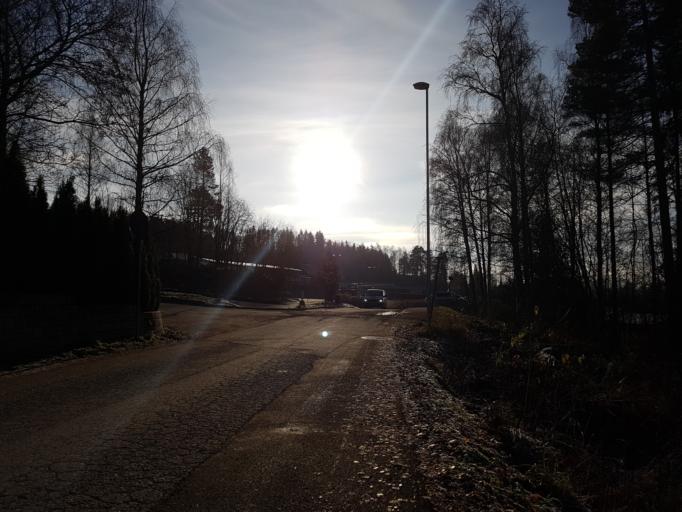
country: NO
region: Oppland
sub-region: Lillehammer
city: Lillehammer
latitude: 61.1143
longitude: 10.4775
